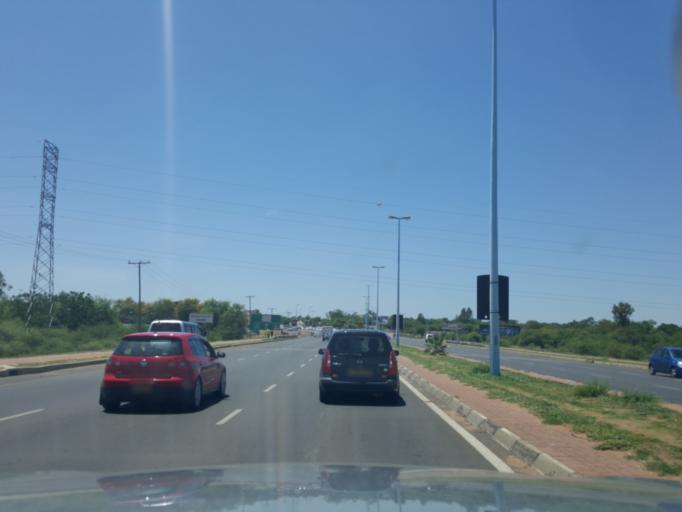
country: BW
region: Kweneng
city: Mogoditshane
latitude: -24.6429
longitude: 25.8825
